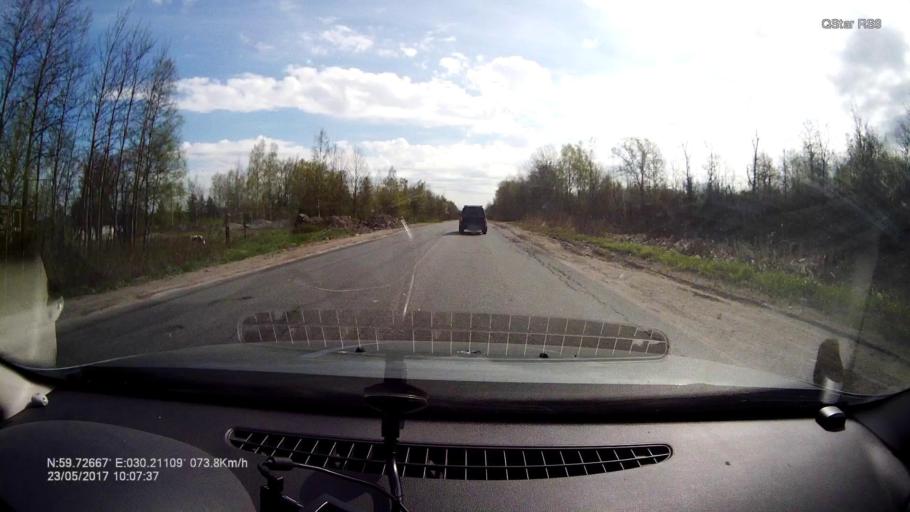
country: RU
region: St.-Petersburg
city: Gorelovo
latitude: 59.7267
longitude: 30.2114
